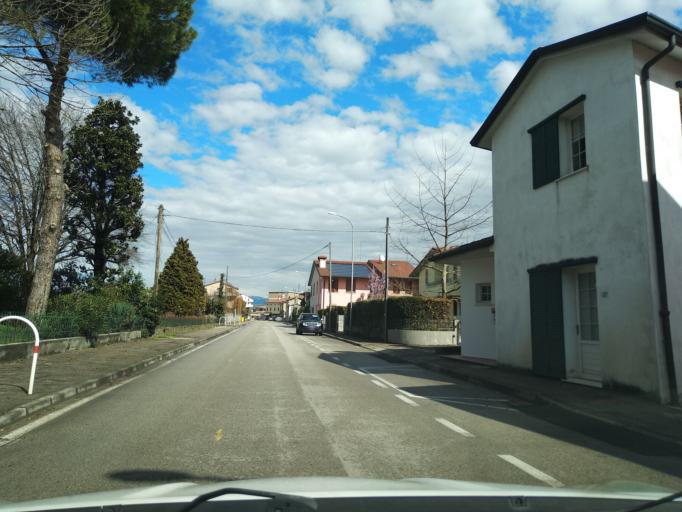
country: IT
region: Veneto
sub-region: Provincia di Vicenza
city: Vigardolo
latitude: 45.6040
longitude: 11.5906
